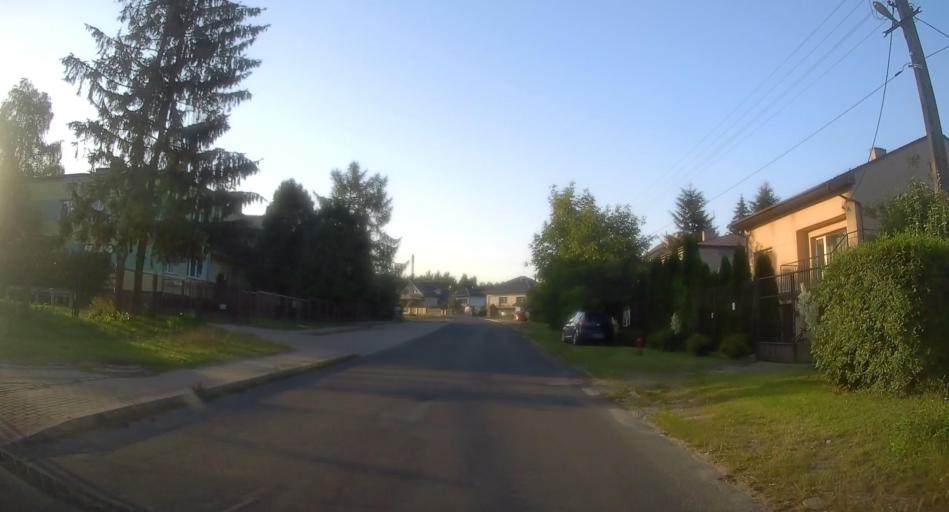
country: PL
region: Lodz Voivodeship
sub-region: Powiat skierniewicki
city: Kowiesy
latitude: 51.8901
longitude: 20.4244
